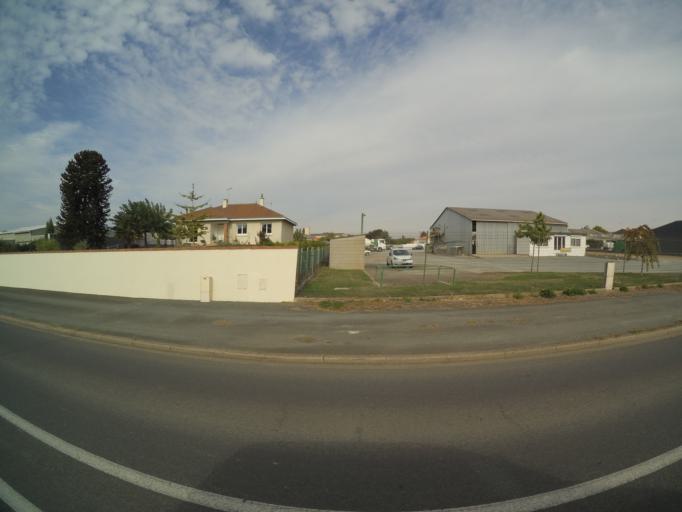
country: FR
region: Pays de la Loire
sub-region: Departement de Maine-et-Loire
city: Jallais
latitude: 47.1988
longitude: -0.8535
